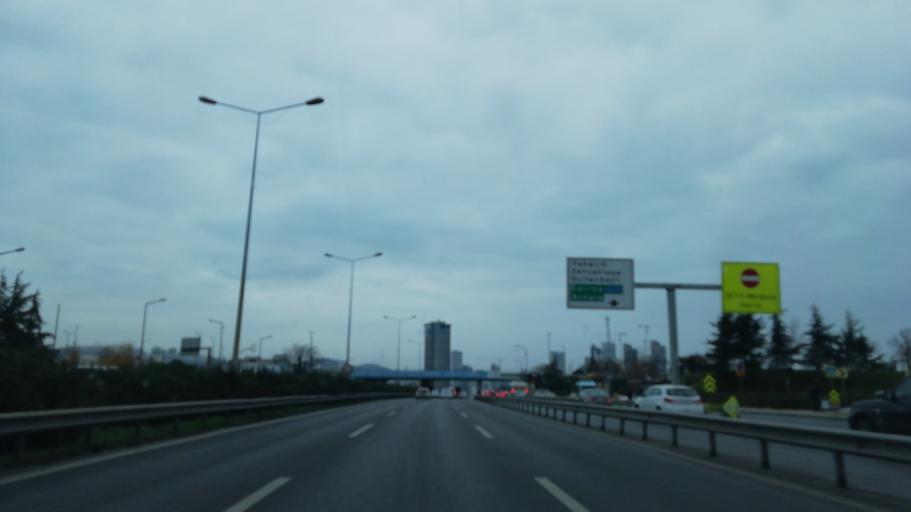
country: TR
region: Istanbul
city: Maltepe
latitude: 40.9070
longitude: 29.2090
